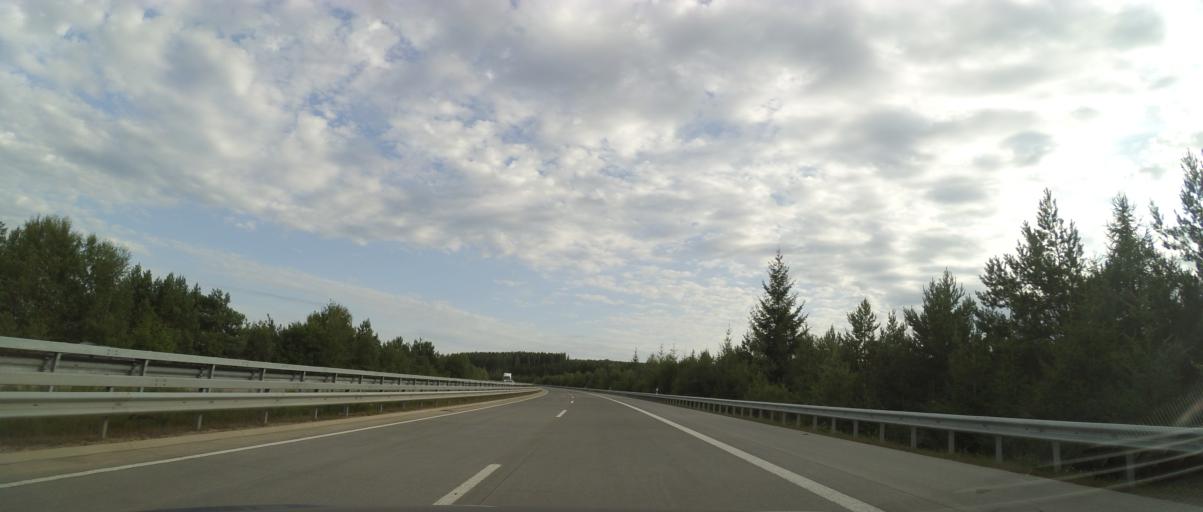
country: DE
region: Rheinland-Pfalz
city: Bescheid
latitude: 49.7266
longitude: 6.8887
